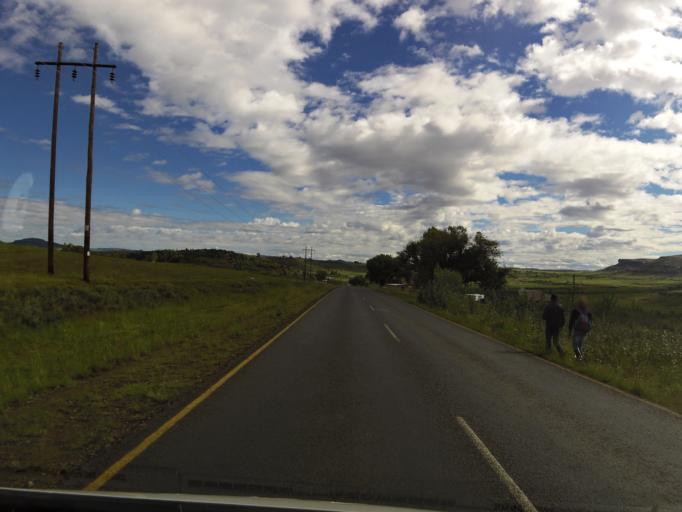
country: LS
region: Berea
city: Teyateyaneng
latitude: -29.2094
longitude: 27.6179
